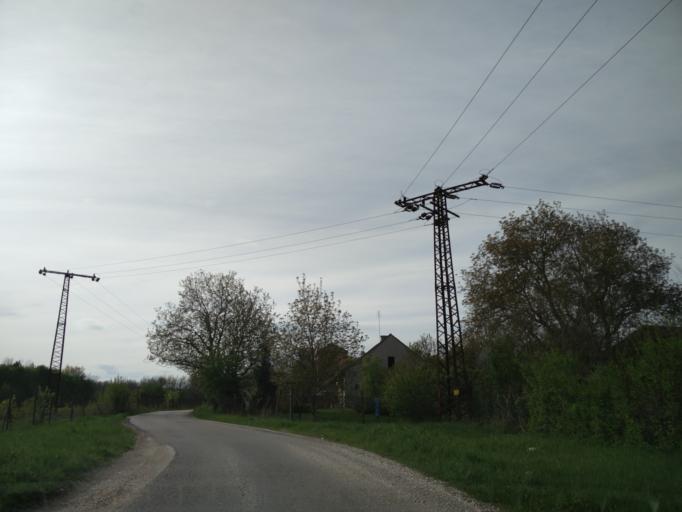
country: HU
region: Zala
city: Zalaegerszeg
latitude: 46.8749
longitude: 16.8559
